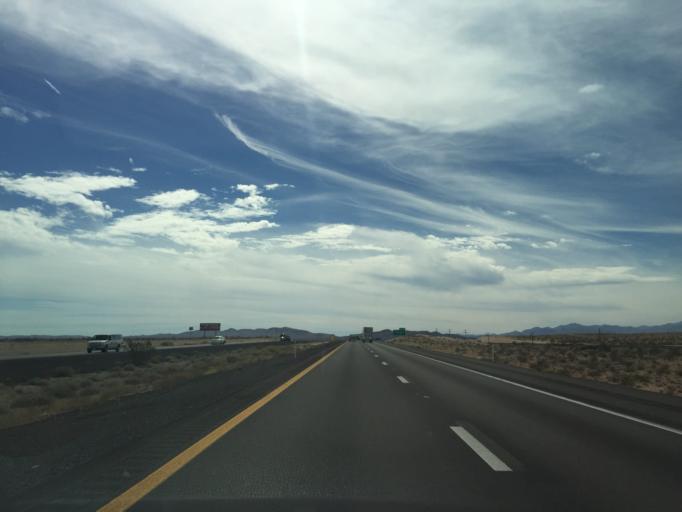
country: US
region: Nevada
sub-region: Clark County
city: Moapa Town
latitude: 36.5109
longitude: -114.7485
